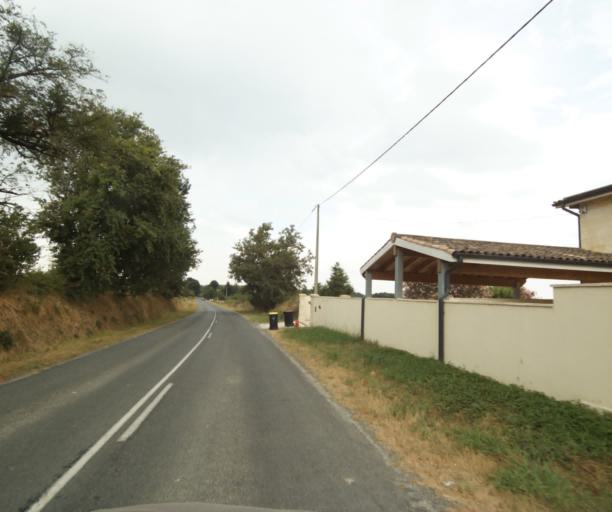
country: FR
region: Aquitaine
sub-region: Departement de la Gironde
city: La Sauve
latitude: 44.7549
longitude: -0.3299
